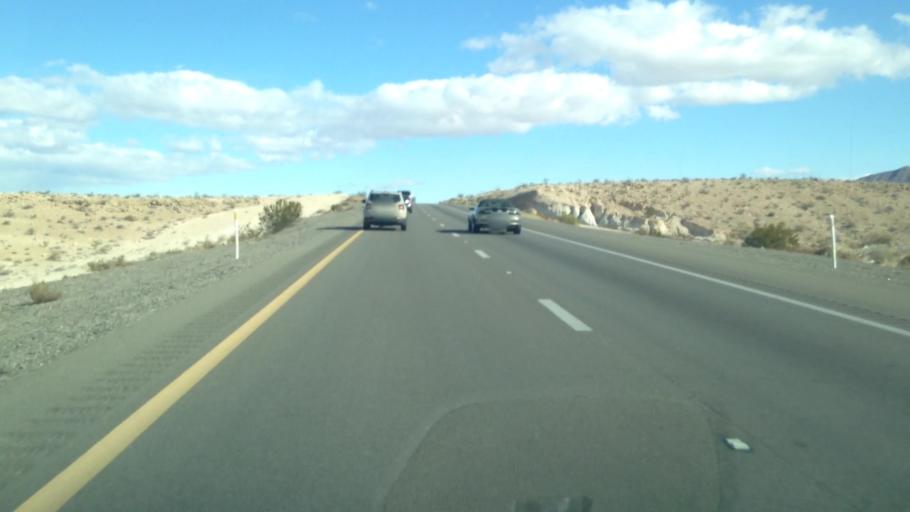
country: US
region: Nevada
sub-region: Clark County
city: Moapa Town
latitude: 36.5682
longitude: -114.6734
